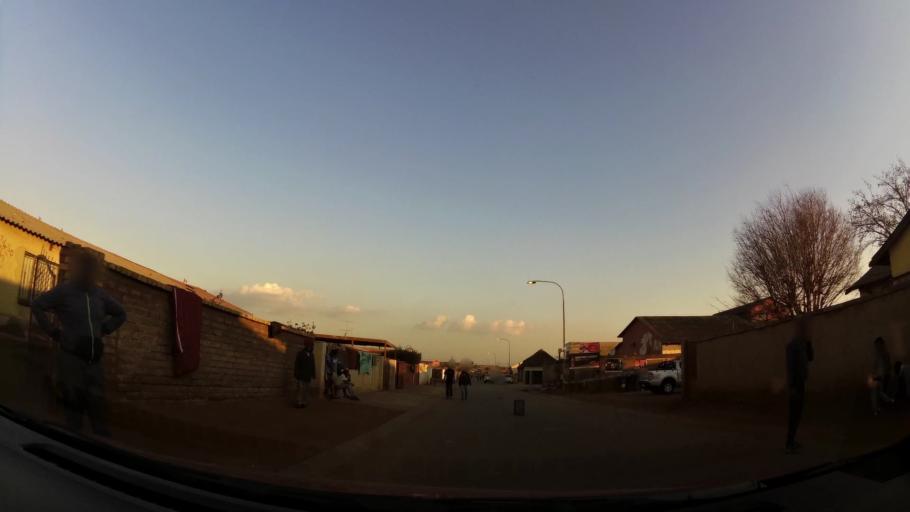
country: ZA
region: Gauteng
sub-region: City of Johannesburg Metropolitan Municipality
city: Soweto
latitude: -26.2197
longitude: 27.8586
